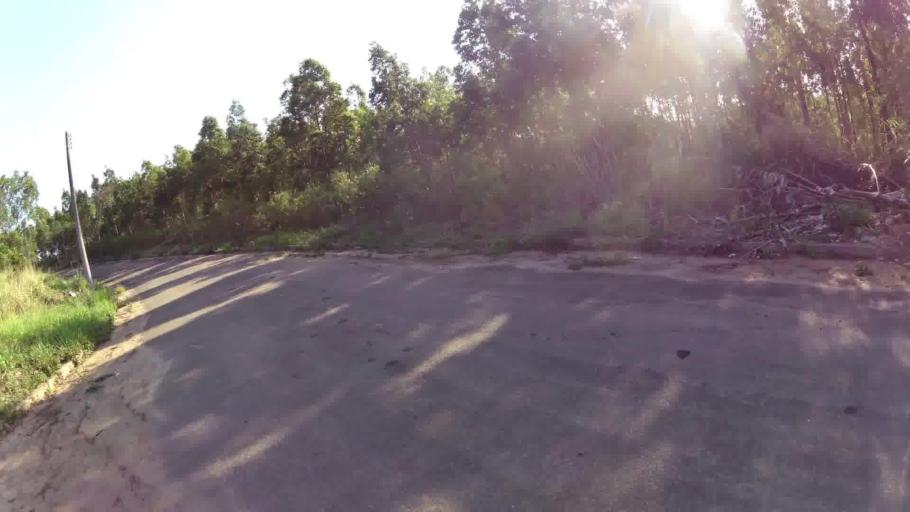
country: BR
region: Espirito Santo
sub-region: Guarapari
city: Guarapari
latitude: -20.7229
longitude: -40.5416
